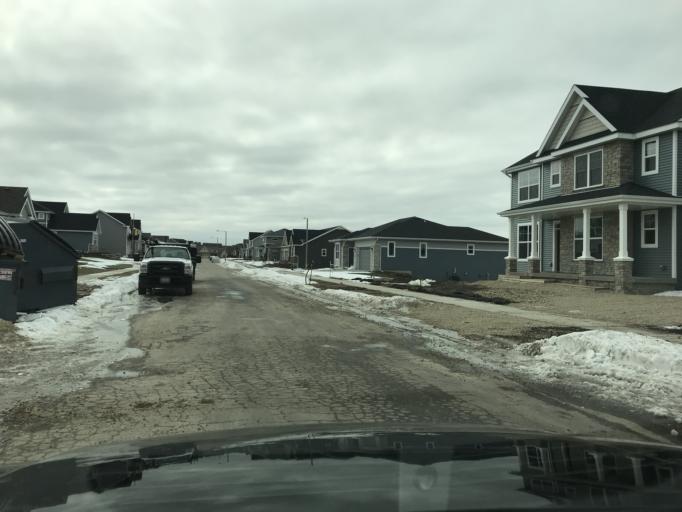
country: US
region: Wisconsin
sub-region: Dane County
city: Monona
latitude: 43.0951
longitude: -89.2723
